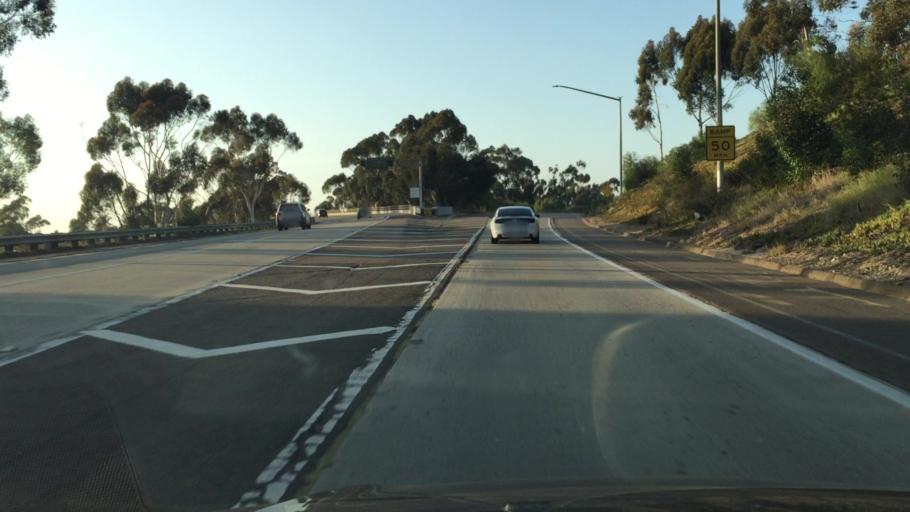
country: US
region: California
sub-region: San Diego County
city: National City
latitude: 32.7161
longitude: -117.1022
